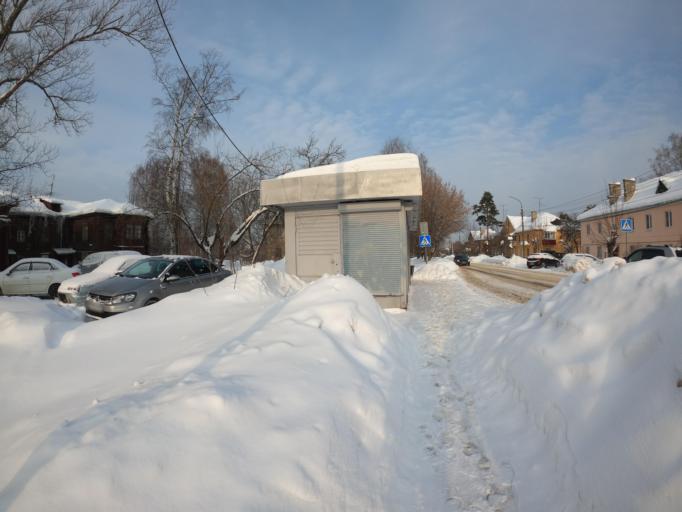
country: RU
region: Moskovskaya
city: Elektrogorsk
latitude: 55.8940
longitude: 38.7698
